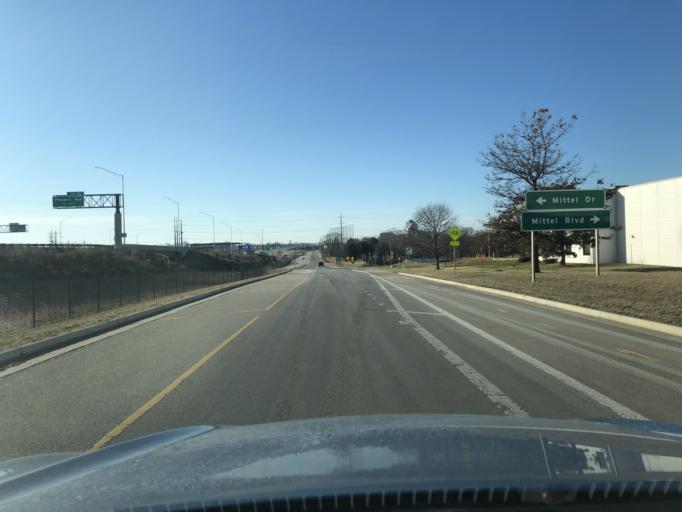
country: US
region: Illinois
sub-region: DuPage County
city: Wood Dale
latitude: 41.9841
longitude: -87.9850
